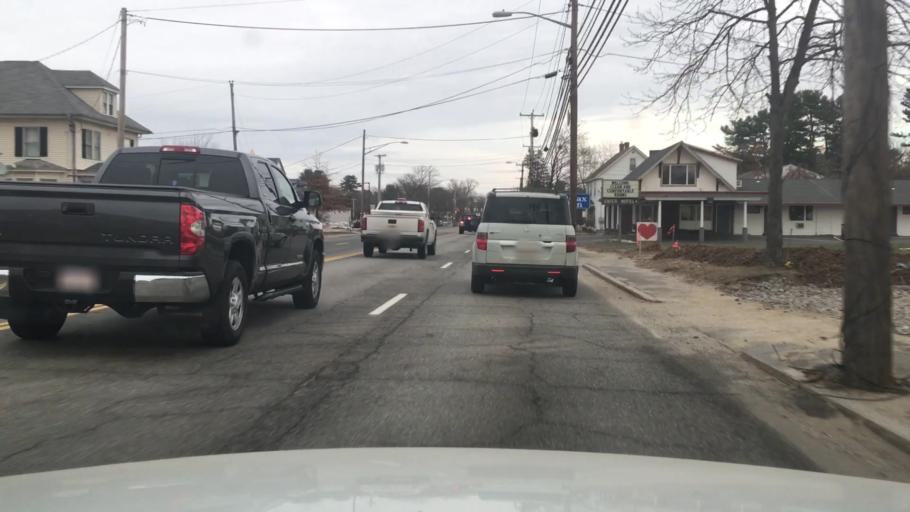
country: US
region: Maine
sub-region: Sagadahoc County
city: Topsham
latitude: 43.9125
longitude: -69.9841
